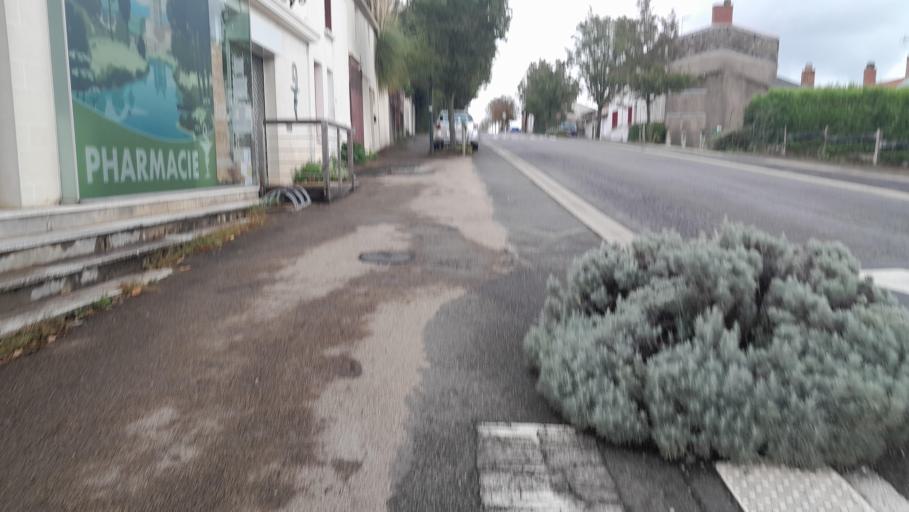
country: FR
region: Pays de la Loire
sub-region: Departement de la Loire-Atlantique
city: Oudon
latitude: 47.3477
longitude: -1.2839
